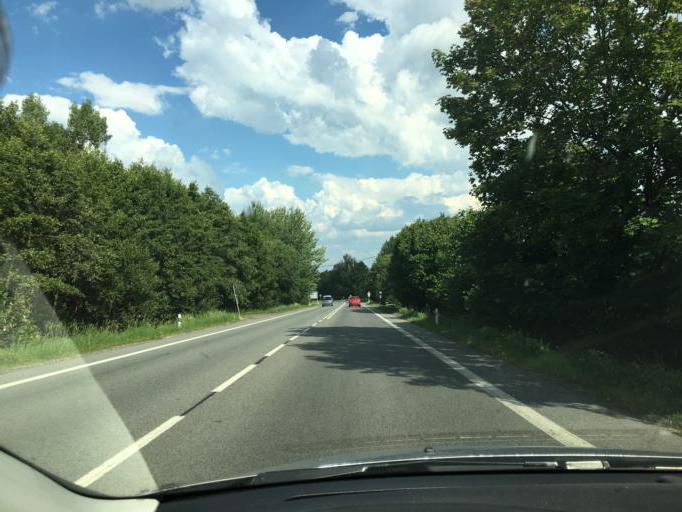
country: CZ
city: Horni Branna
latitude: 50.6198
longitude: 15.5839
